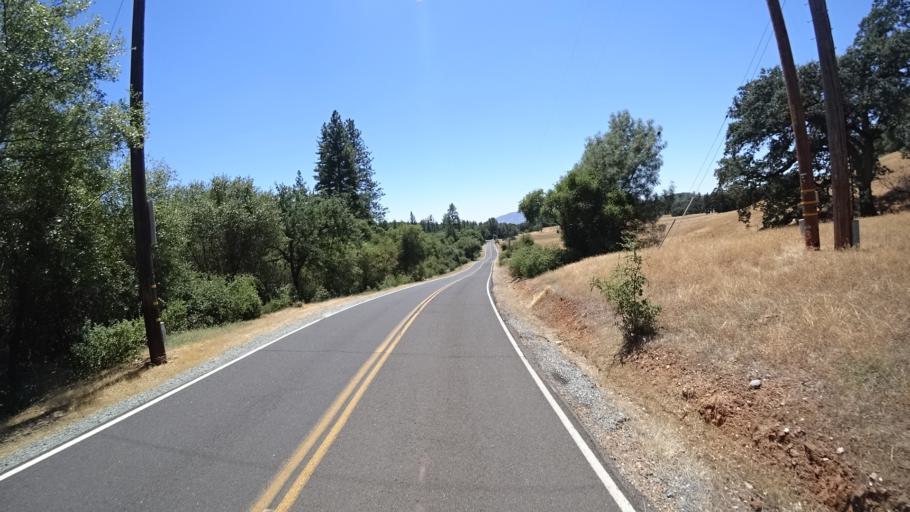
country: US
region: California
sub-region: Calaveras County
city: Murphys
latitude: 38.1355
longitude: -120.4967
